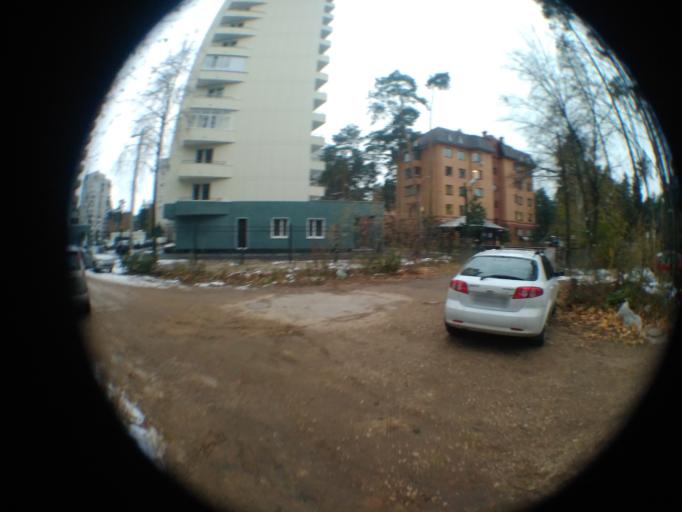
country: RU
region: Moskovskaya
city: Zhukovskiy
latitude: 55.5856
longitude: 38.1385
